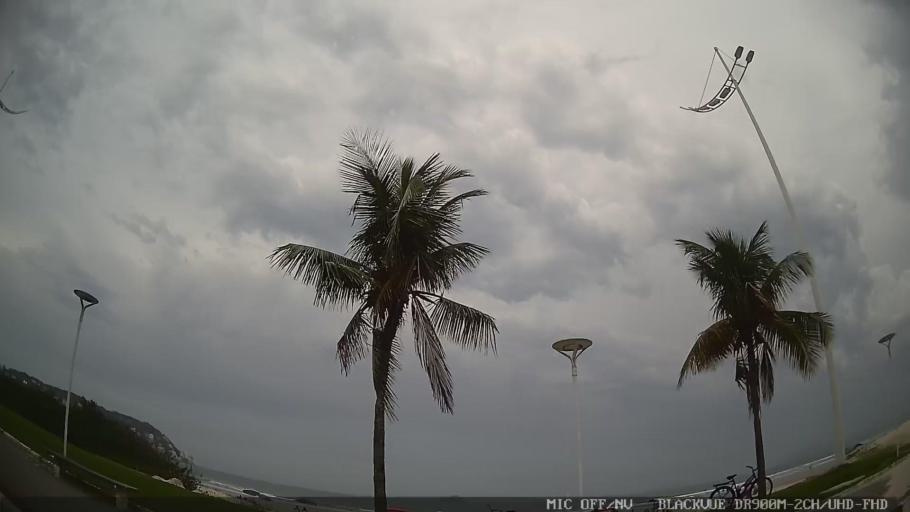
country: BR
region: Sao Paulo
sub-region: Guaruja
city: Guaruja
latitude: -23.9850
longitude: -46.2126
